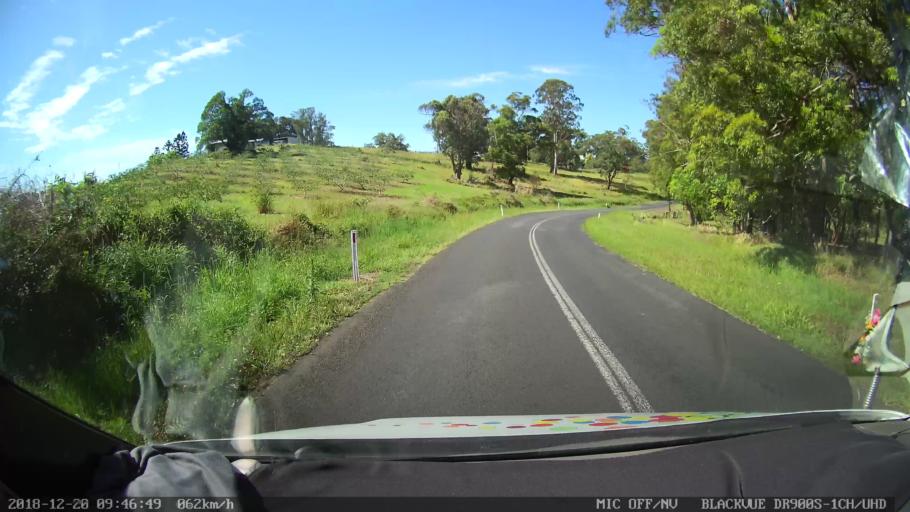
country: AU
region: New South Wales
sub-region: Lismore Municipality
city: Goonellabah
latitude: -28.7576
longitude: 153.3017
